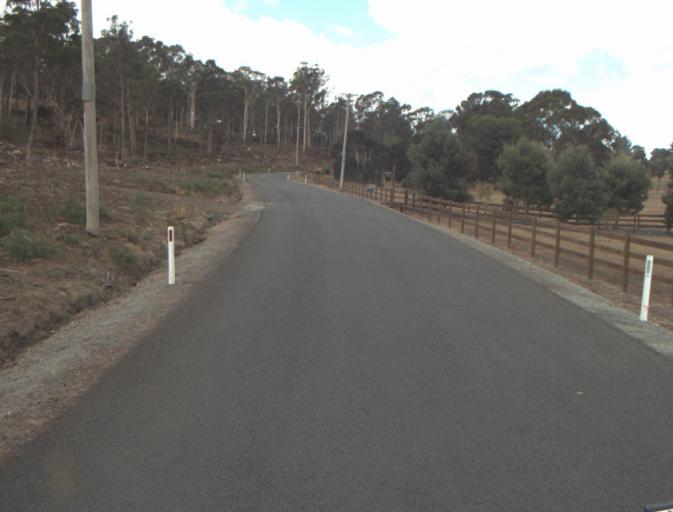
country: AU
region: Tasmania
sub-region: Launceston
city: Mayfield
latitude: -41.2825
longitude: 147.0321
